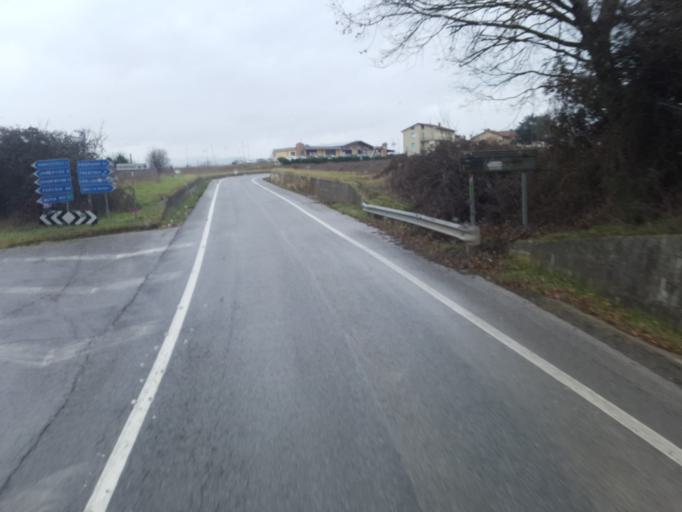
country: IT
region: Umbria
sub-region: Provincia di Perugia
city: Trestina
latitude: 43.3646
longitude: 12.2708
